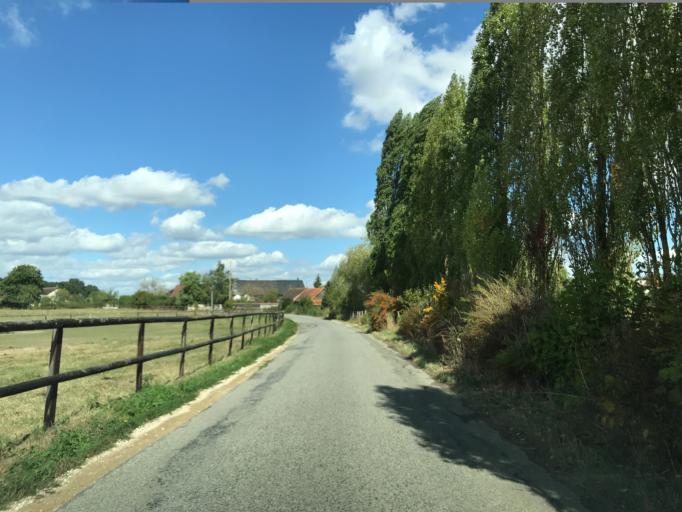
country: FR
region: Haute-Normandie
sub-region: Departement de l'Eure
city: La Chapelle-Reanville
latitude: 49.1027
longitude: 1.3899
